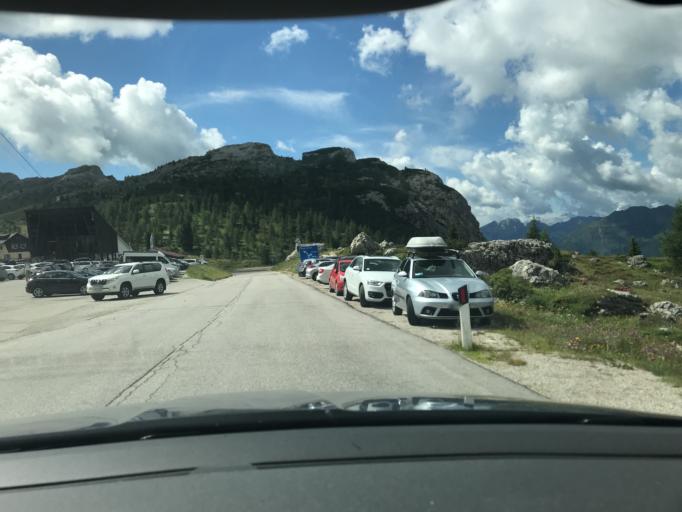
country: IT
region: Veneto
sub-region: Provincia di Belluno
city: Livinallongo del Col di Lana
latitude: 46.5202
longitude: 12.0077
